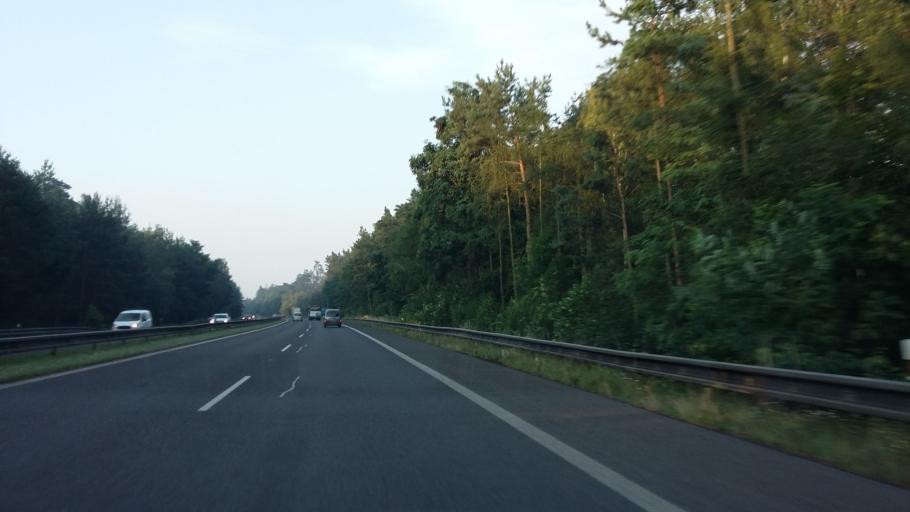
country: CZ
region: Central Bohemia
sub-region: Okres Mlada Boleslav
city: Mlada Boleslav
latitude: 50.3543
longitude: 14.8719
